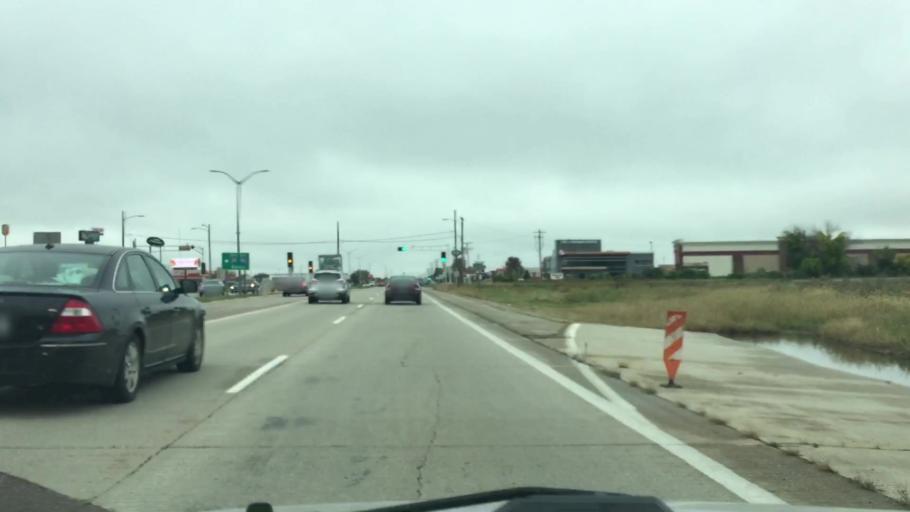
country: US
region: Wisconsin
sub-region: Rock County
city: Janesville
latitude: 42.7256
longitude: -88.9933
